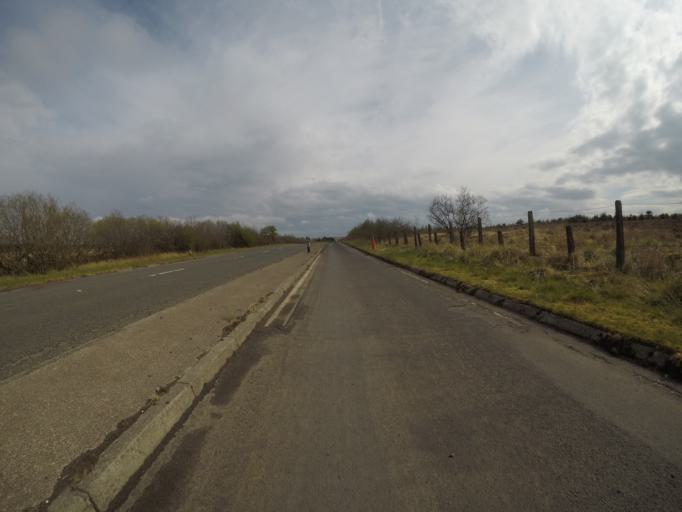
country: GB
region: Scotland
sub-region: East Renfrewshire
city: Neilston
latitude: 55.7012
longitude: -4.3956
